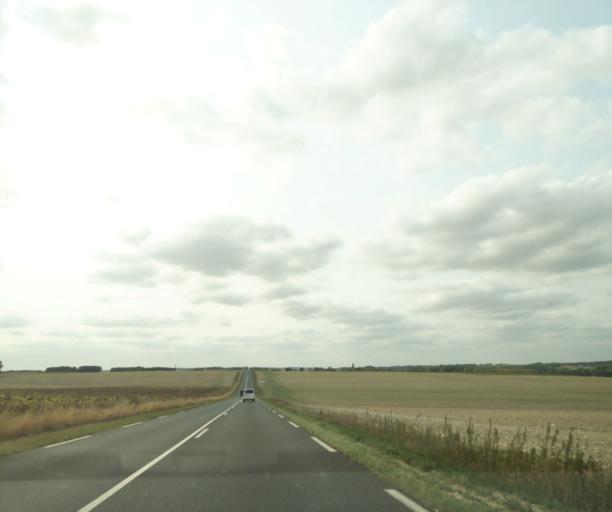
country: FR
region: Centre
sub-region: Departement de l'Indre
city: Clion
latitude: 46.9253
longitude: 1.2873
